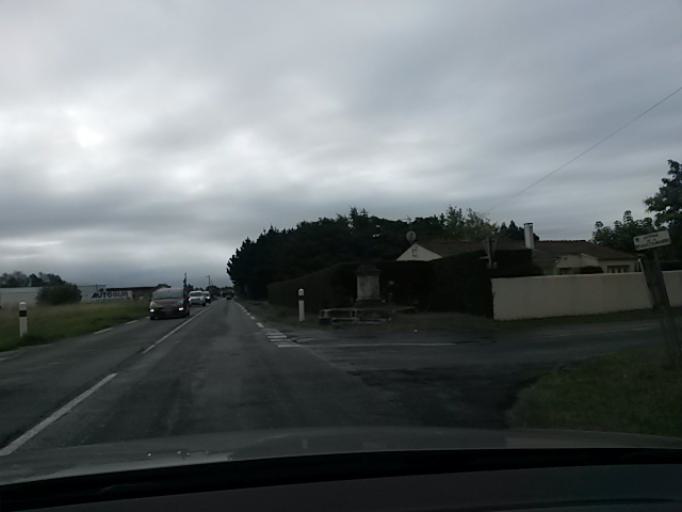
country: FR
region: Poitou-Charentes
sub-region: Departement de la Charente-Maritime
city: Saint-Trojan-les-Bains
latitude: 45.8814
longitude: -1.2227
